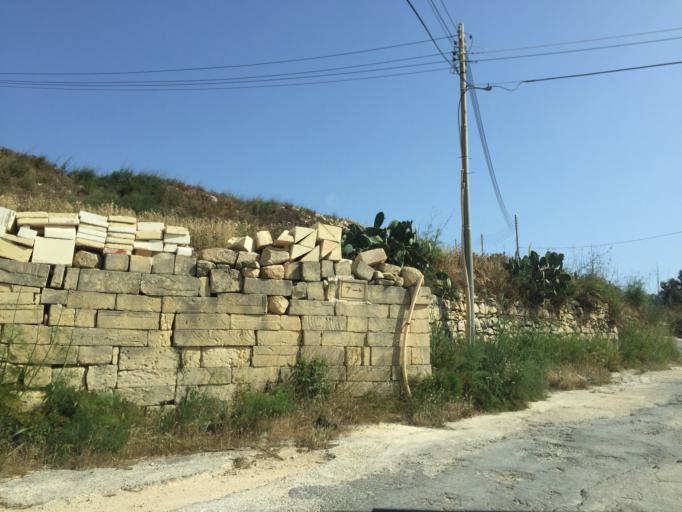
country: MT
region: L-Gharb
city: Gharb
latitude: 36.0667
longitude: 14.2060
